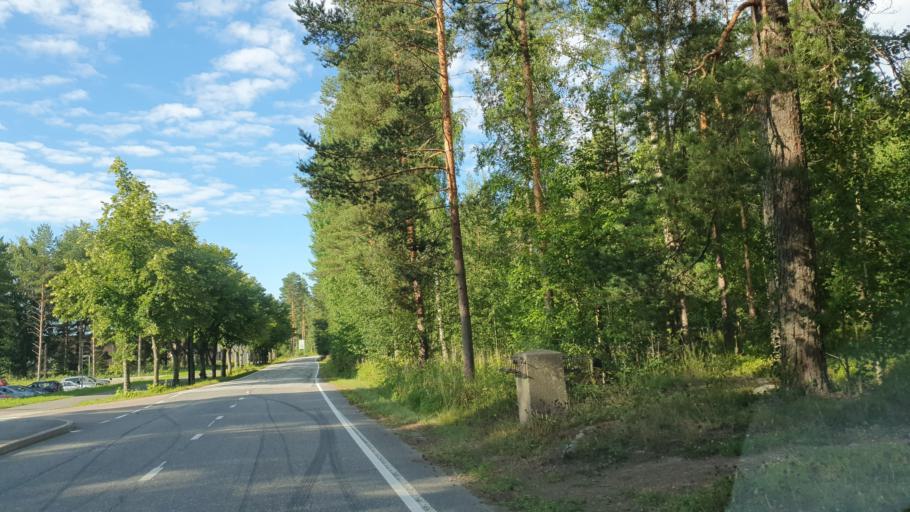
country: FI
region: Central Finland
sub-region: Jyvaeskylae
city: Saeynaetsalo
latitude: 62.1572
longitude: 25.7631
